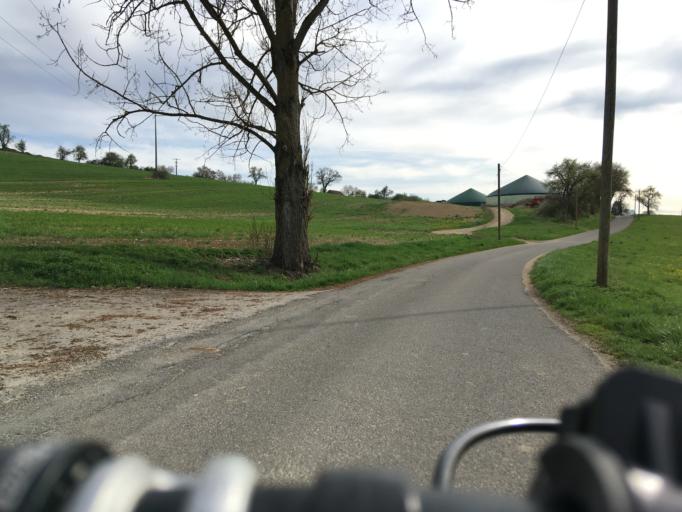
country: CH
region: Schaffhausen
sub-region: Bezirk Reiat
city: Thayngen
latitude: 47.7992
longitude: 8.7305
